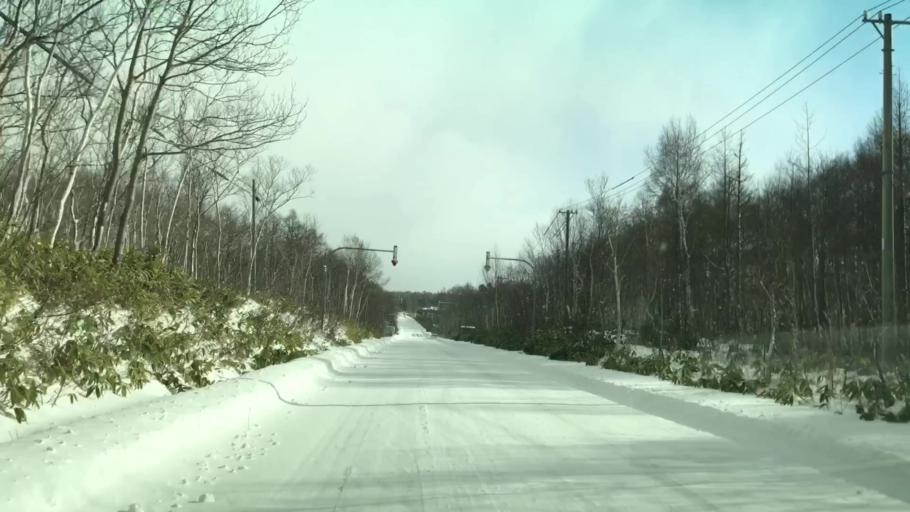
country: JP
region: Hokkaido
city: Yoichi
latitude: 43.3187
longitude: 140.5257
